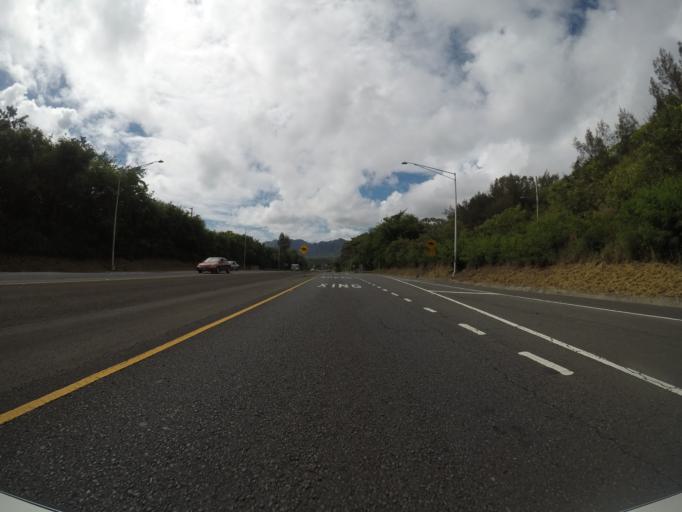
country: US
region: Hawaii
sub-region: Honolulu County
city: Waimanalo
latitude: 21.3588
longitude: -157.7337
